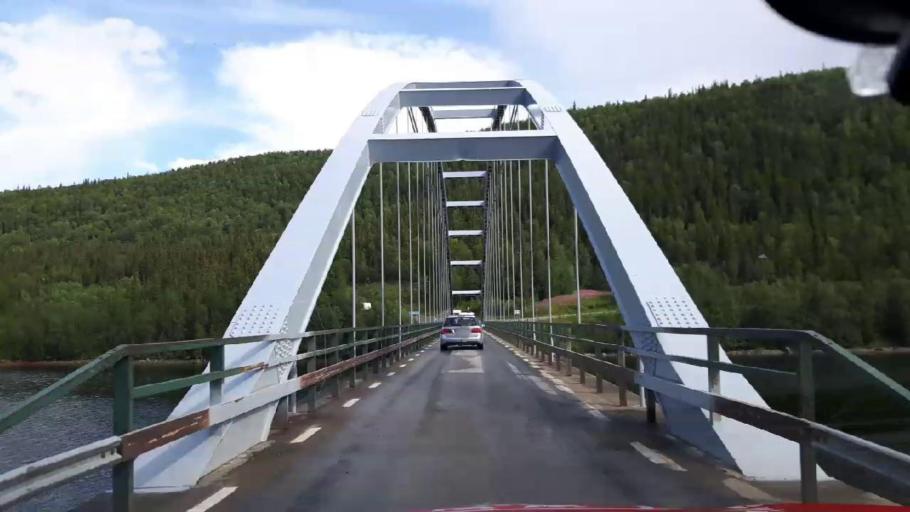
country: SE
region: Vaesterbotten
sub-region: Vilhelmina Kommun
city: Sjoberg
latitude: 65.0313
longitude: 15.1391
